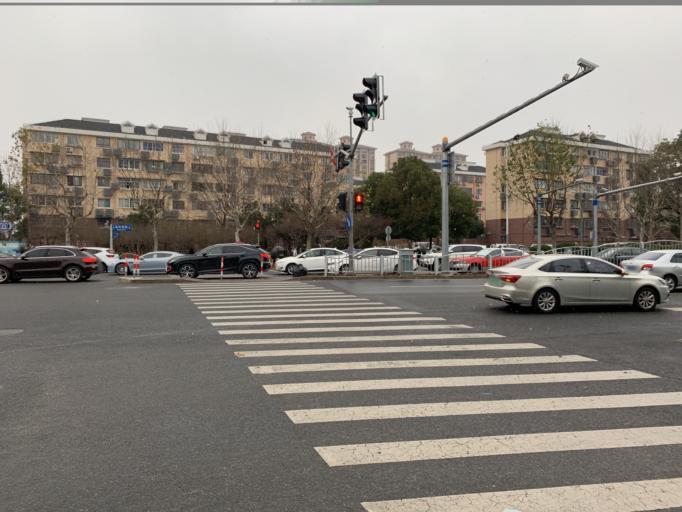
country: CN
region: Shanghai Shi
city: Huamu
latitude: 31.1895
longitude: 121.5298
